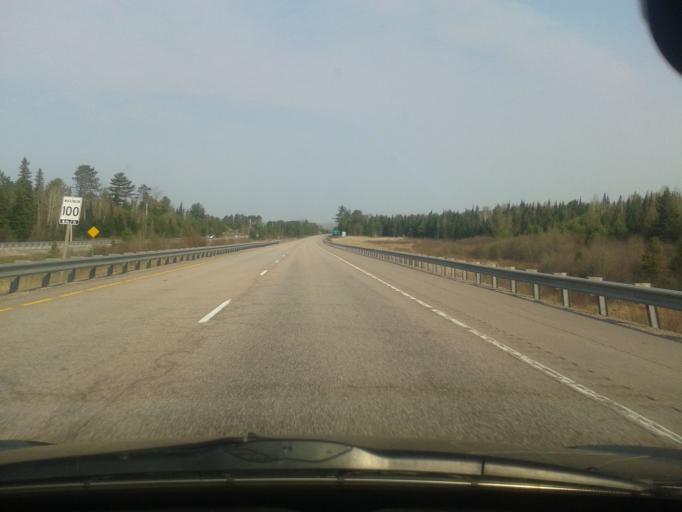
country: CA
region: Ontario
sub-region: Nipissing District
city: North Bay
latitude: 46.2510
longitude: -79.3717
